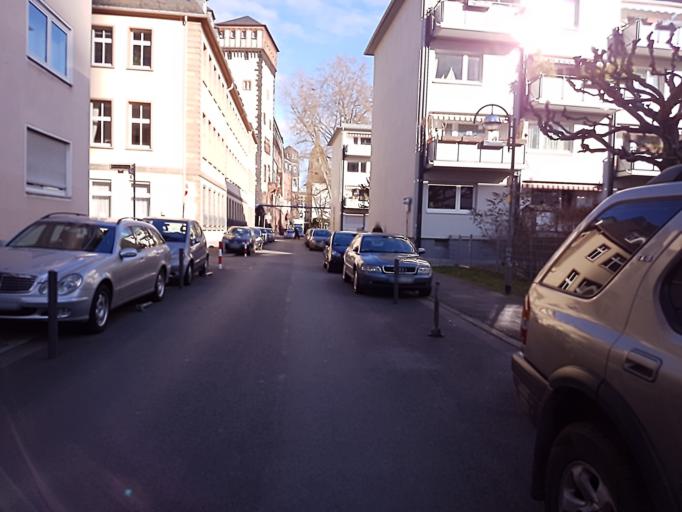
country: DE
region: Hesse
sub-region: Regierungsbezirk Darmstadt
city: Frankfurt am Main
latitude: 50.1097
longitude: 8.6785
